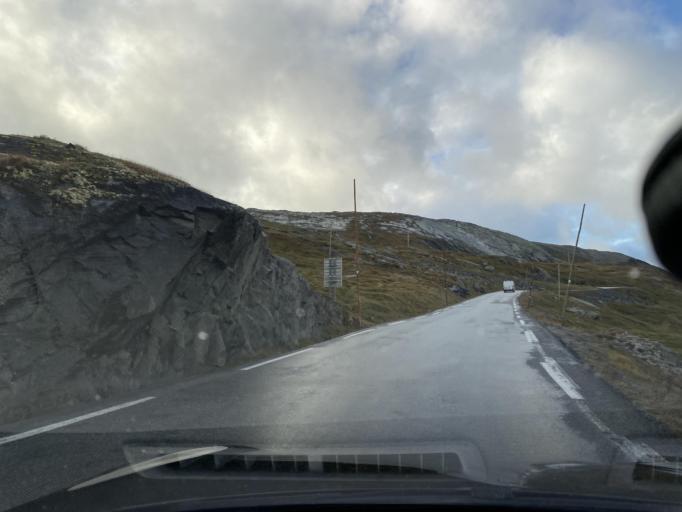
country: NO
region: Sogn og Fjordane
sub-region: Ardal
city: Farnes
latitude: 61.5710
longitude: 8.0301
